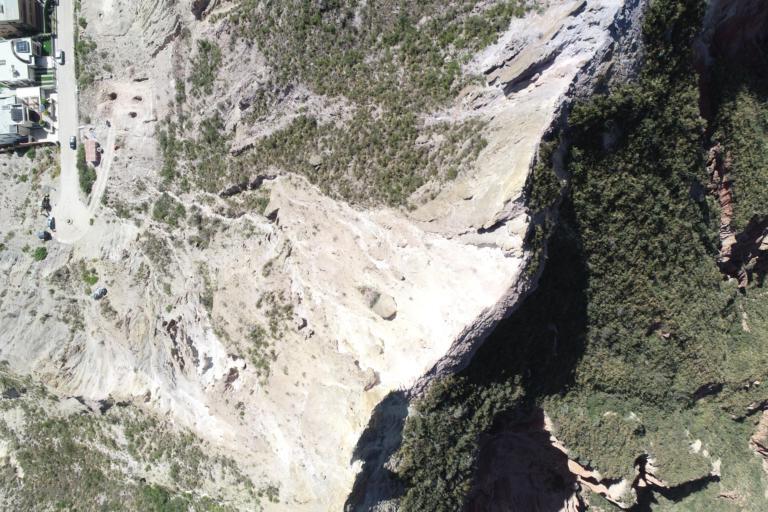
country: BO
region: La Paz
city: La Paz
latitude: -16.5565
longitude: -68.0825
